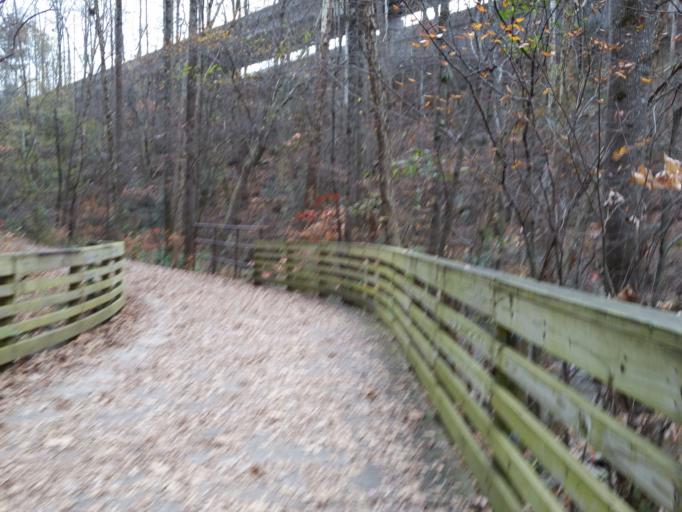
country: US
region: Georgia
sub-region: Cobb County
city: Vinings
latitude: 33.8801
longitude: -84.4511
